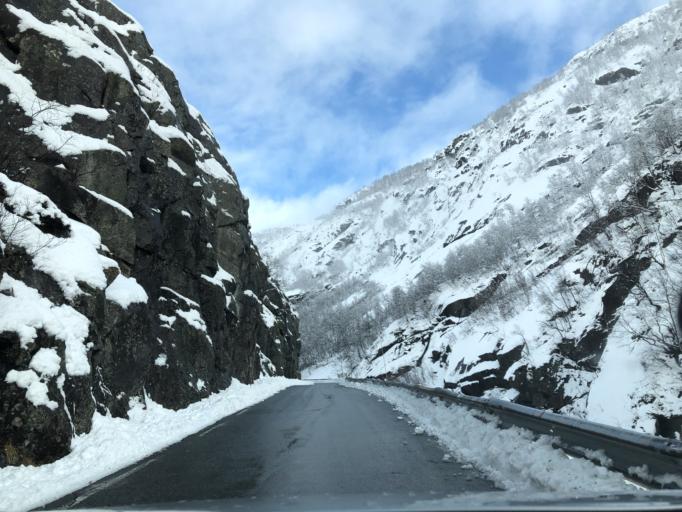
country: NO
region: Rogaland
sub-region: Sauda
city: Sauda
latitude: 59.7254
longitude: 6.7324
